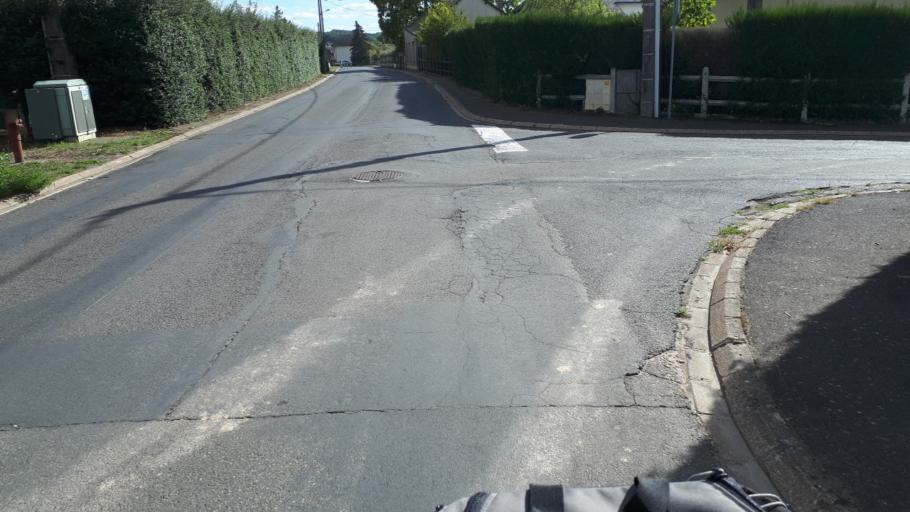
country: FR
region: Centre
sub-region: Departement du Loir-et-Cher
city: Villiers-sur-Loir
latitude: 47.7932
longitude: 0.9615
